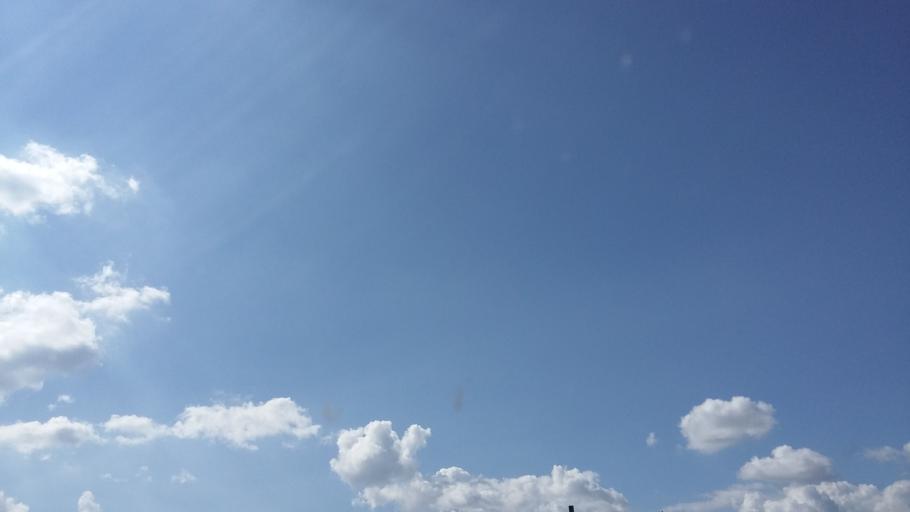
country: DE
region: Bavaria
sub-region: Swabia
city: Holzheim
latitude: 48.3530
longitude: 10.0998
